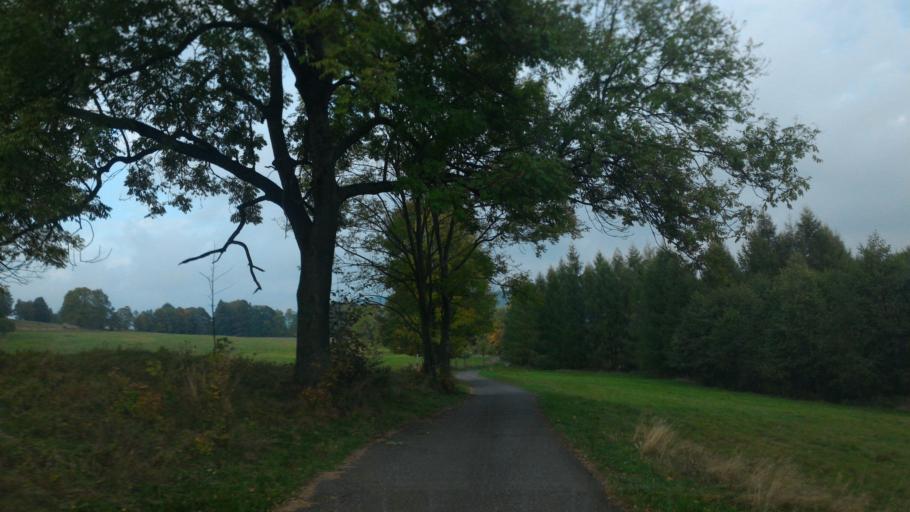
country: CZ
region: Ustecky
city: Dolni Podluzi
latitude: 50.8657
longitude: 14.5741
